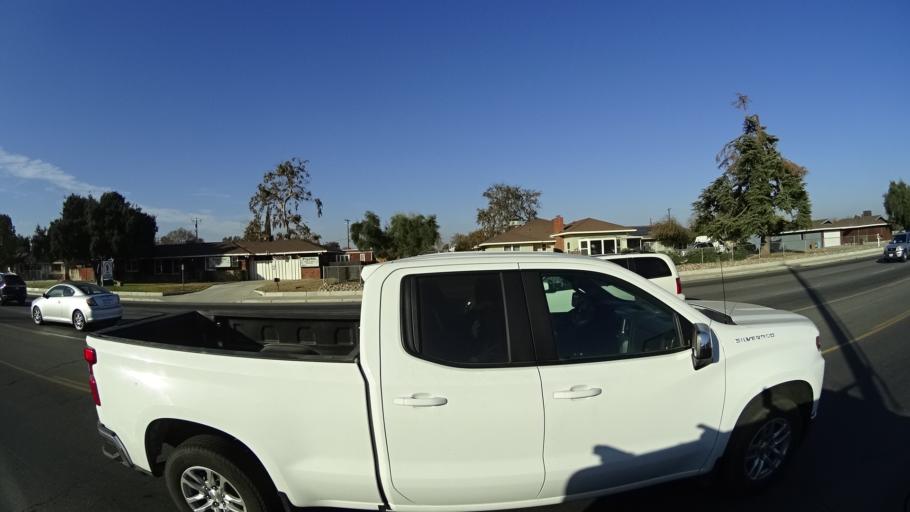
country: US
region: California
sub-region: Kern County
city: Bakersfield
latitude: 35.3393
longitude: -119.0265
